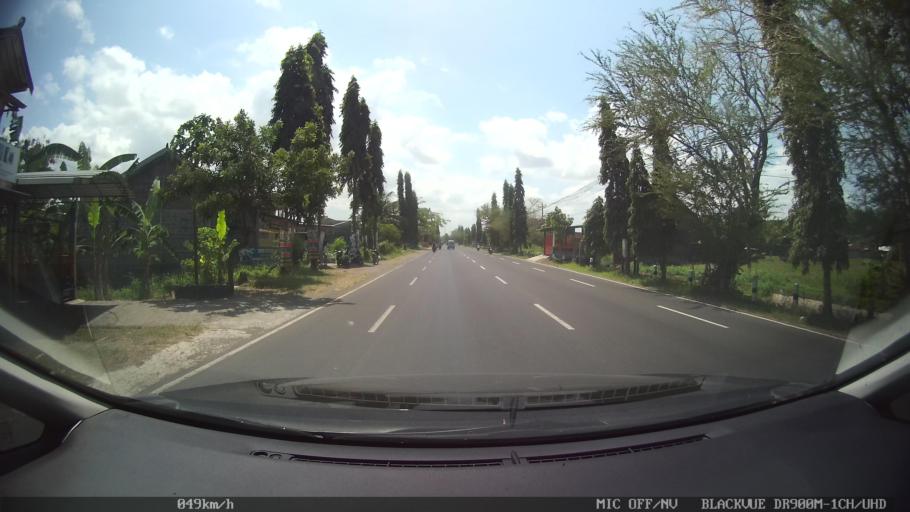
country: ID
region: Daerah Istimewa Yogyakarta
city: Pandak
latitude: -7.9272
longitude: 110.2769
